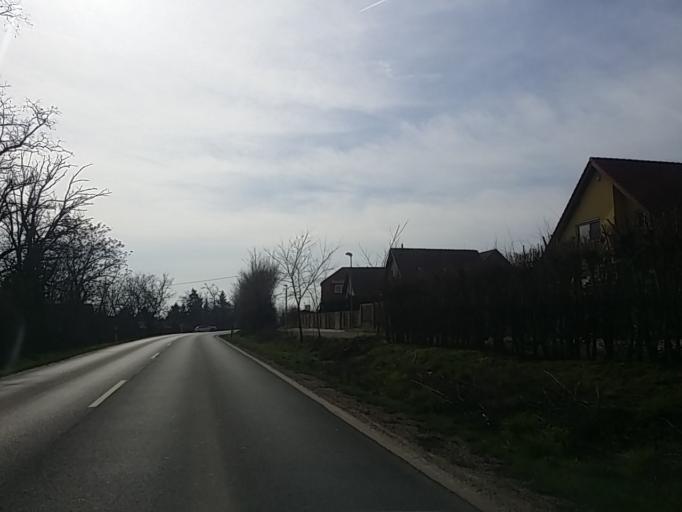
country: HU
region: Pest
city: Fot
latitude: 47.6223
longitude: 19.1987
